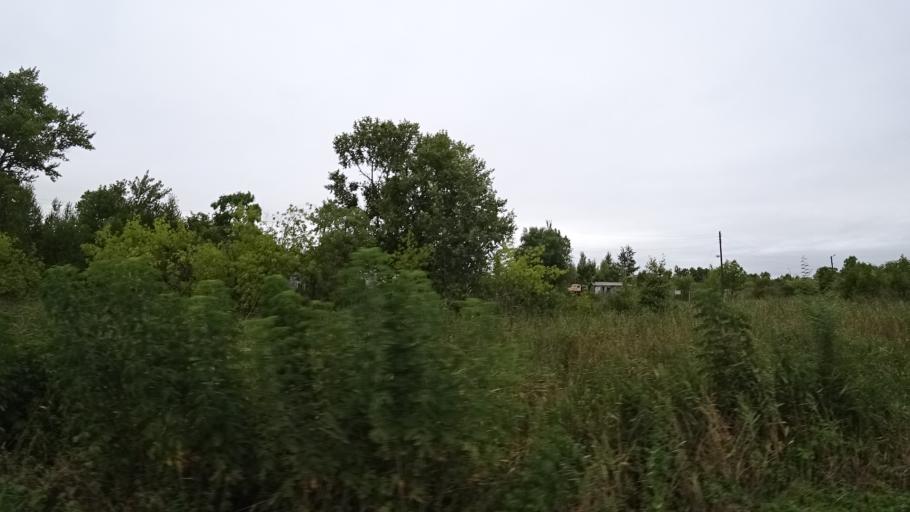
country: RU
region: Primorskiy
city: Chernigovka
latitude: 44.3371
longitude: 132.5276
